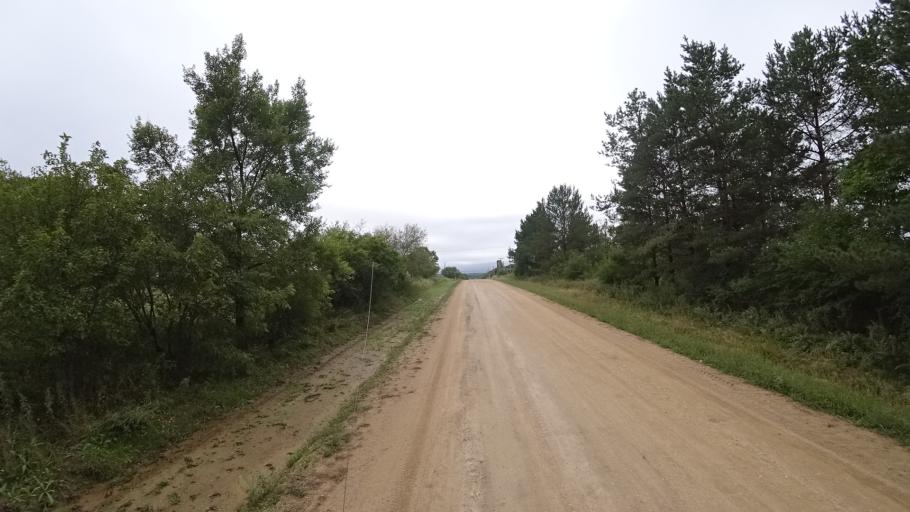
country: RU
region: Primorskiy
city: Monastyrishche
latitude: 44.0785
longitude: 132.5905
